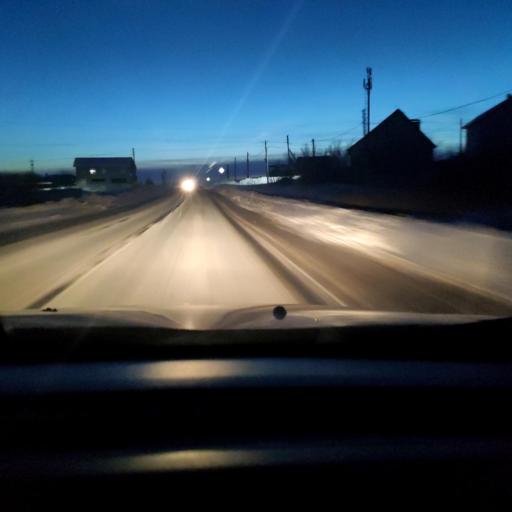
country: RU
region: Samara
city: Kinel'
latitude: 53.2711
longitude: 50.6039
